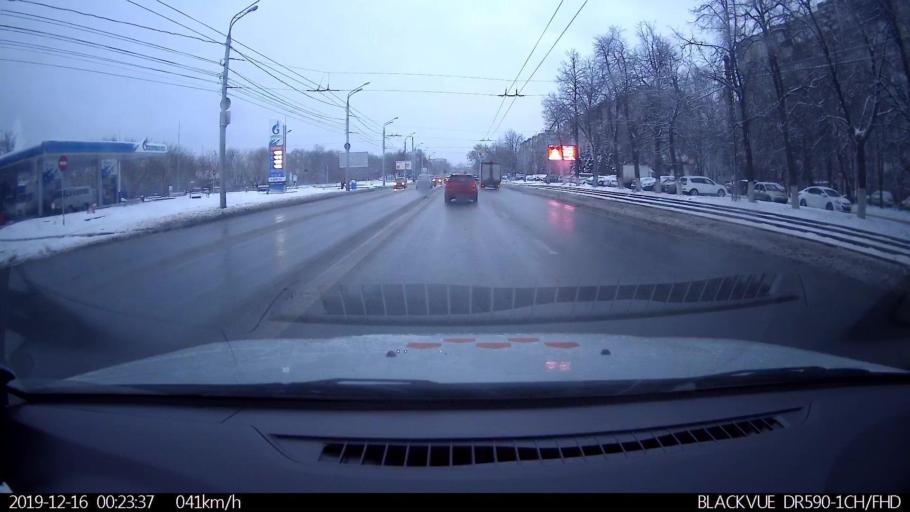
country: RU
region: Nizjnij Novgorod
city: Neklyudovo
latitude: 56.3405
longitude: 43.8797
